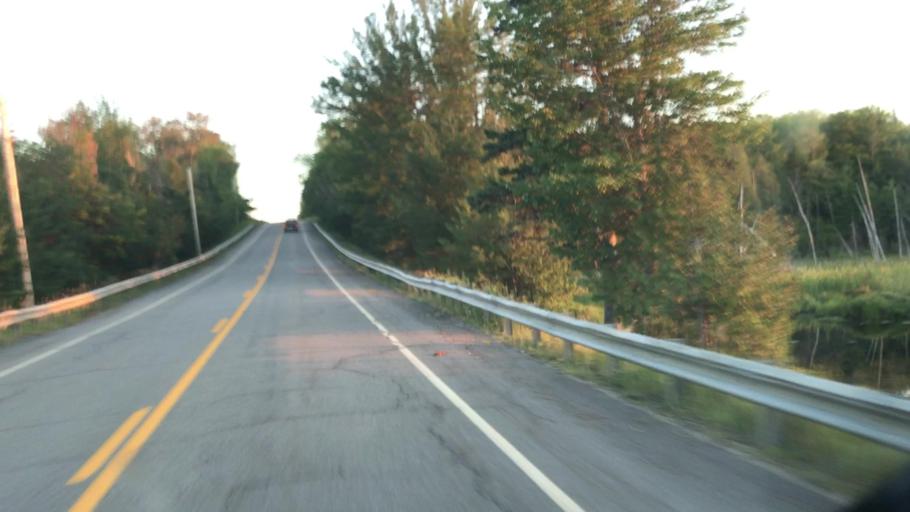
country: US
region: Maine
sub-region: Penobscot County
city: Medway
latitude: 45.5974
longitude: -68.3106
